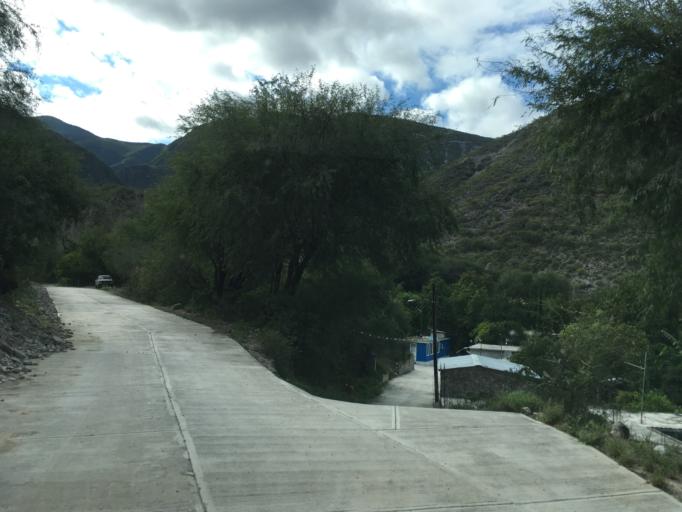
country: MX
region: Hidalgo
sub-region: Metztitlan
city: Fontezuelas
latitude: 20.6390
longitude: -98.9262
